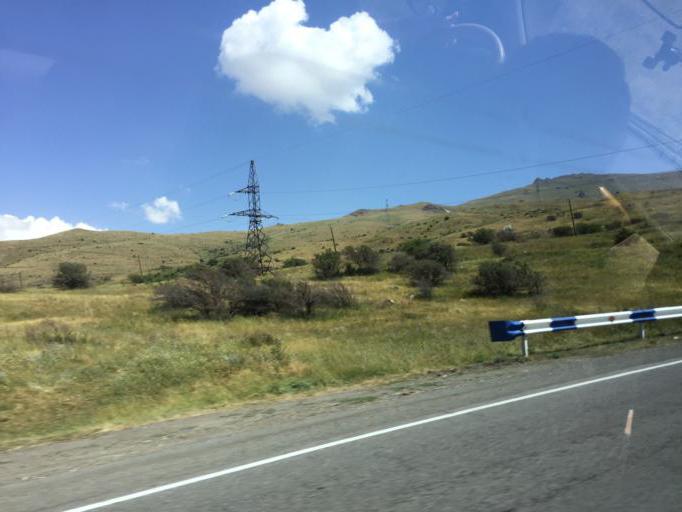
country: AM
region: Vayots' Dzori Marz
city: Jermuk
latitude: 39.7055
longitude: 45.6848
